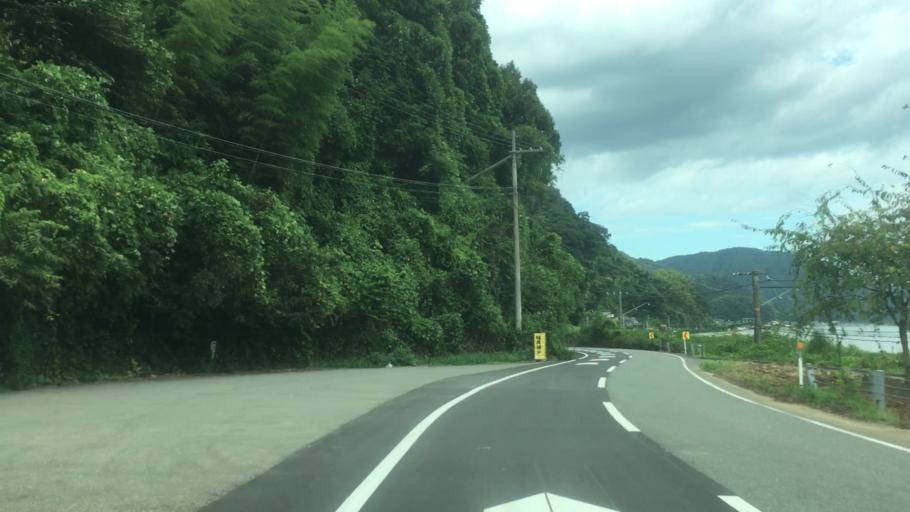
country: JP
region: Hyogo
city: Toyooka
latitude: 35.5792
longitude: 134.8000
